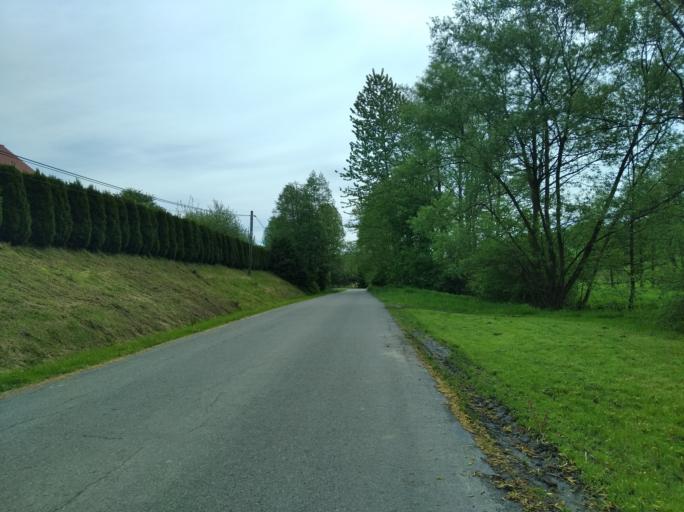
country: PL
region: Subcarpathian Voivodeship
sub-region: Powiat strzyzowski
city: Strzyzow
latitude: 49.9273
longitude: 21.7662
